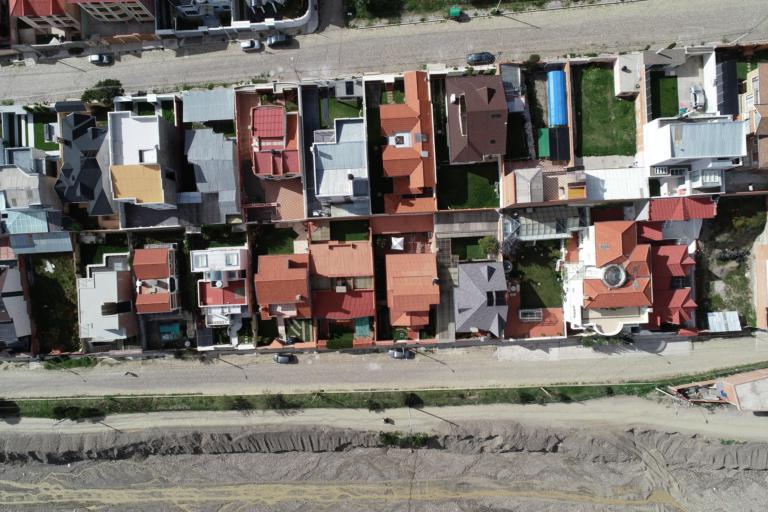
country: BO
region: La Paz
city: La Paz
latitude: -16.5020
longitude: -68.0765
